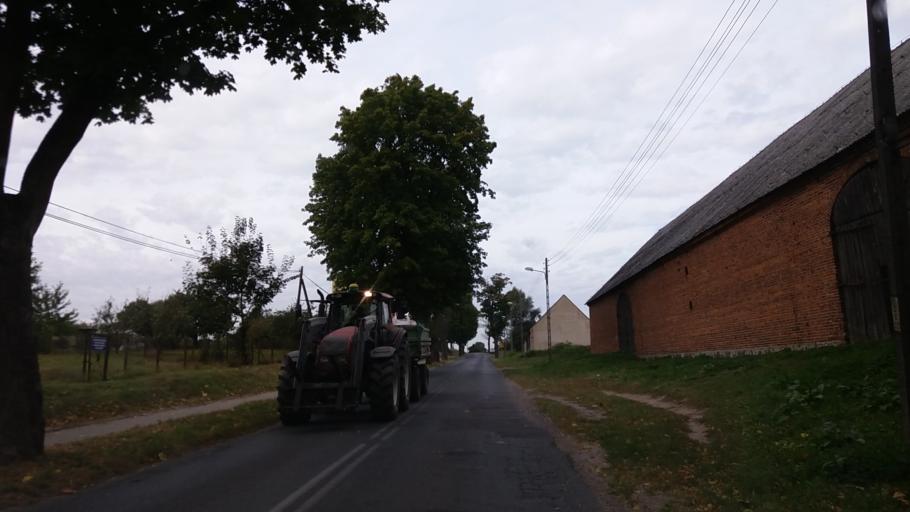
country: PL
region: Lubusz
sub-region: Powiat strzelecko-drezdenecki
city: Strzelce Krajenskie
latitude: 52.9096
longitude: 15.5015
